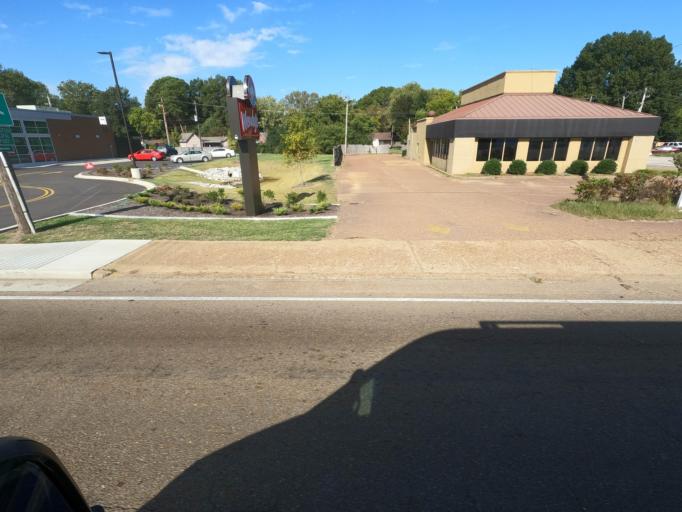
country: US
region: Tennessee
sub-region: Shelby County
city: Millington
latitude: 35.3421
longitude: -89.9094
